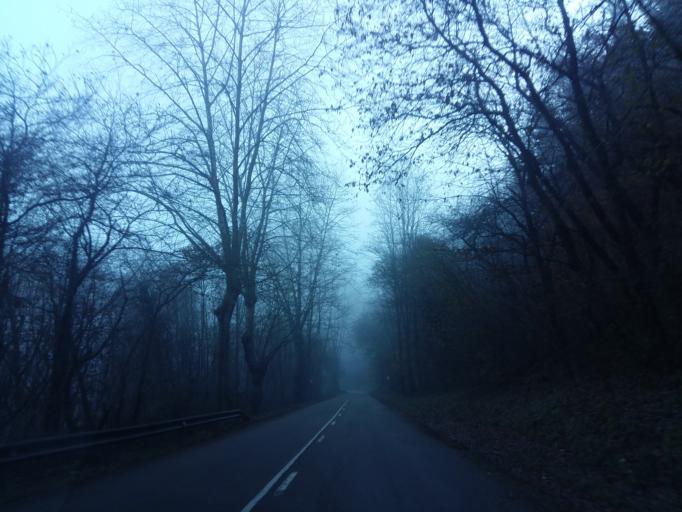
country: ES
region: Cantabria
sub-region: Provincia de Cantabria
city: Arredondo
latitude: 43.2758
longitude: -3.5844
